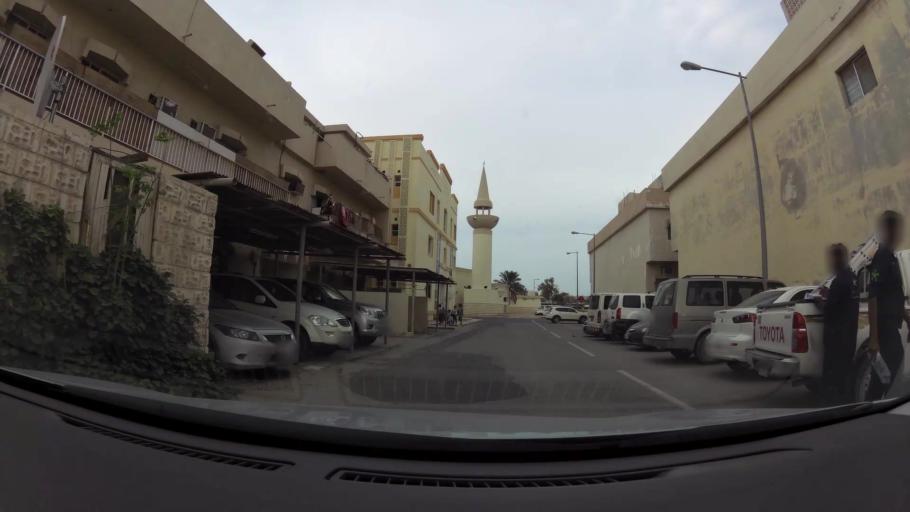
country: QA
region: Baladiyat ad Dawhah
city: Doha
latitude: 25.3184
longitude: 51.4913
